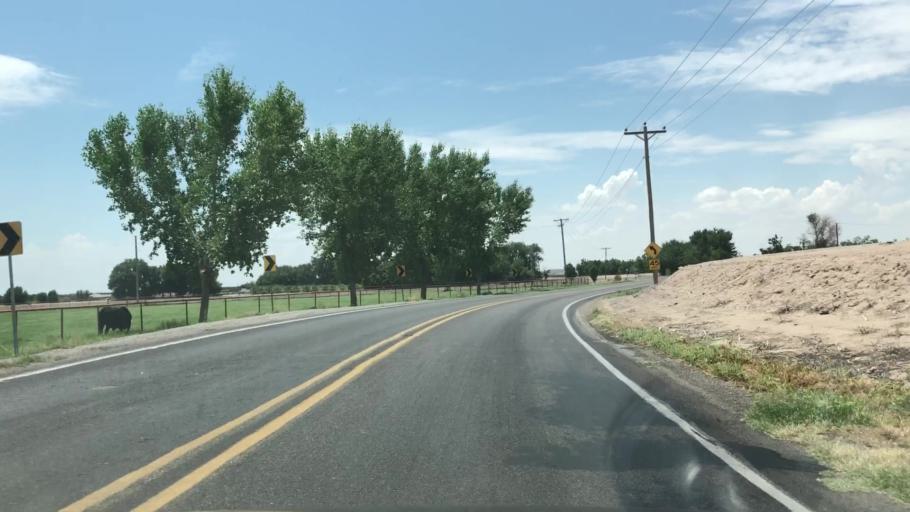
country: US
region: New Mexico
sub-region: Dona Ana County
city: Vado
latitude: 32.0913
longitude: -106.6826
